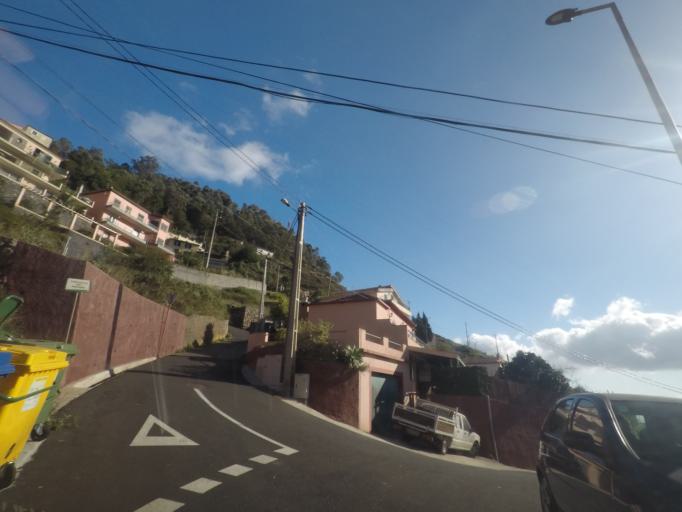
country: PT
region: Madeira
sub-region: Ribeira Brava
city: Campanario
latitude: 32.6623
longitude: -17.0050
